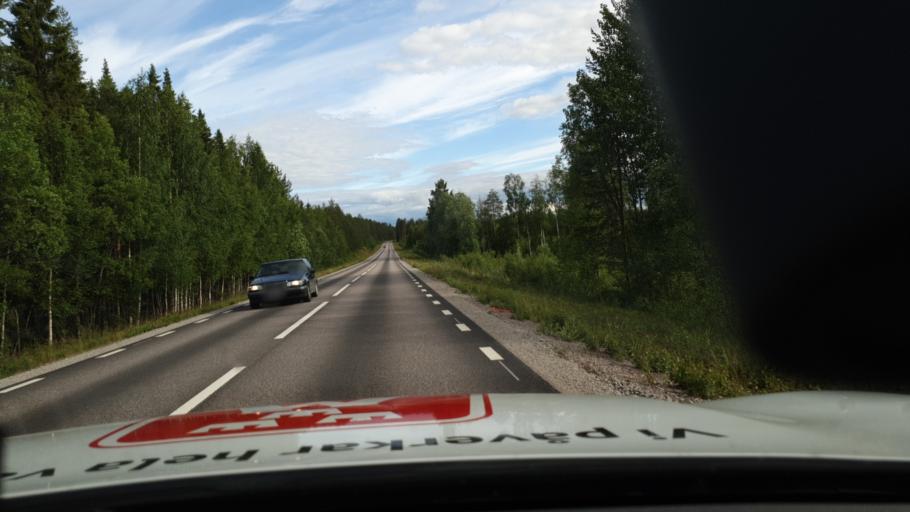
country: SE
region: Norrbotten
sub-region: Overkalix Kommun
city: OEverkalix
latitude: 66.4027
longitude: 22.8087
